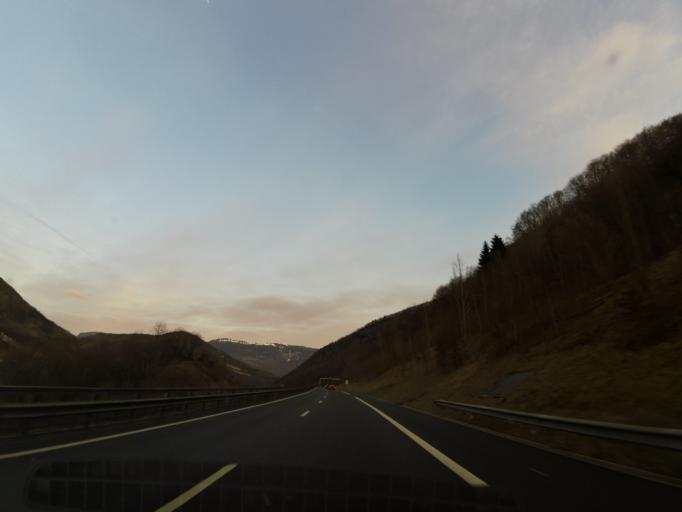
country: FR
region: Rhone-Alpes
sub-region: Departement de l'Ain
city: Chatillon-en-Michaille
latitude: 46.1633
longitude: 5.7597
